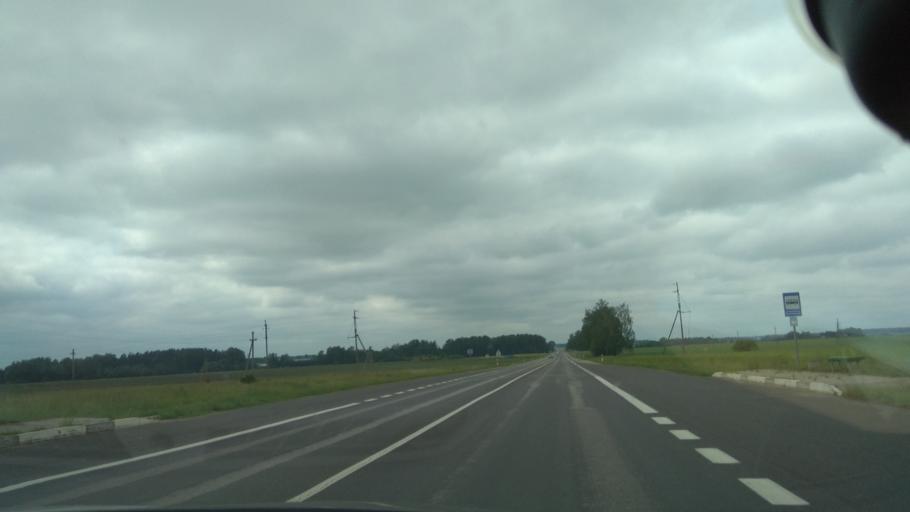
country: LT
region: Panevezys
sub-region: Panevezys City
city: Panevezys
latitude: 55.7504
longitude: 24.1423
